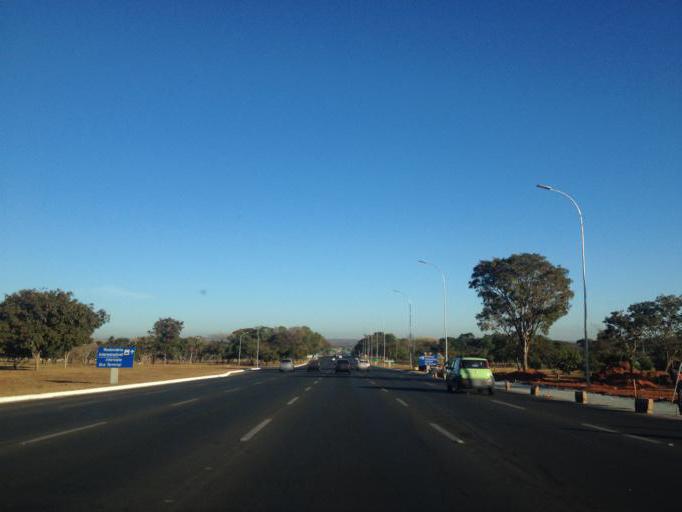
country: BR
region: Federal District
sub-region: Brasilia
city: Brasilia
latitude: -15.7796
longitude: -47.9250
